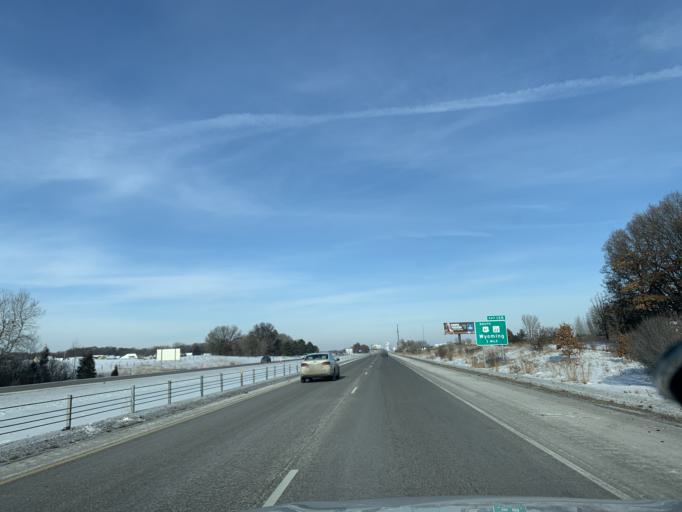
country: US
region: Minnesota
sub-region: Chisago County
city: Wyoming
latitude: 45.3206
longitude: -93.0032
